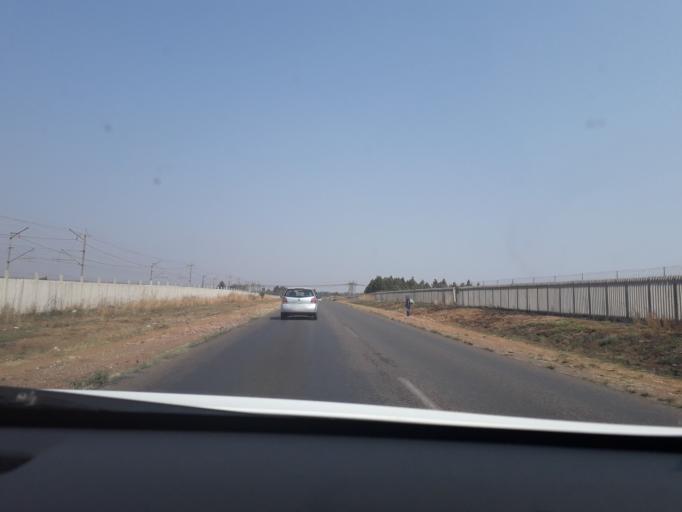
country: ZA
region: Gauteng
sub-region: City of Tshwane Metropolitan Municipality
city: Centurion
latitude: -25.9033
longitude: 28.2258
